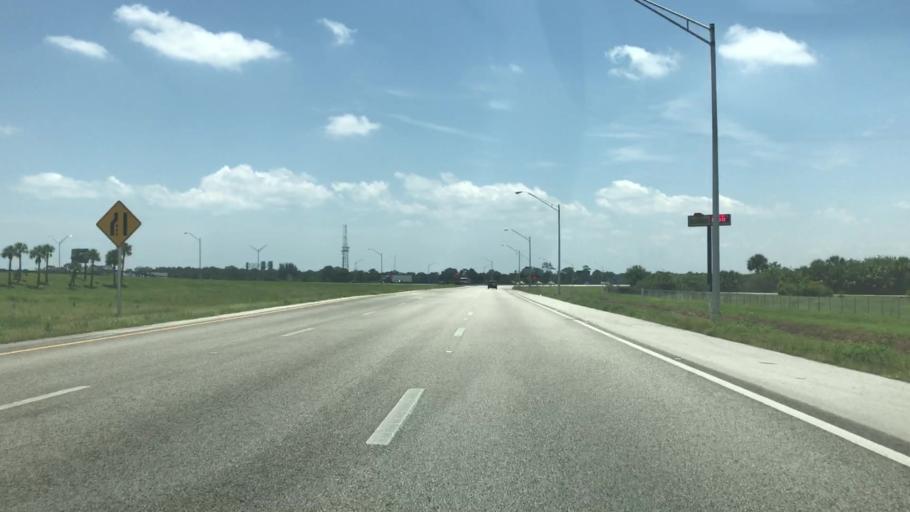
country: US
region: Florida
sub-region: Saint Lucie County
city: Lakewood Park
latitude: 27.4455
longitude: -80.3952
